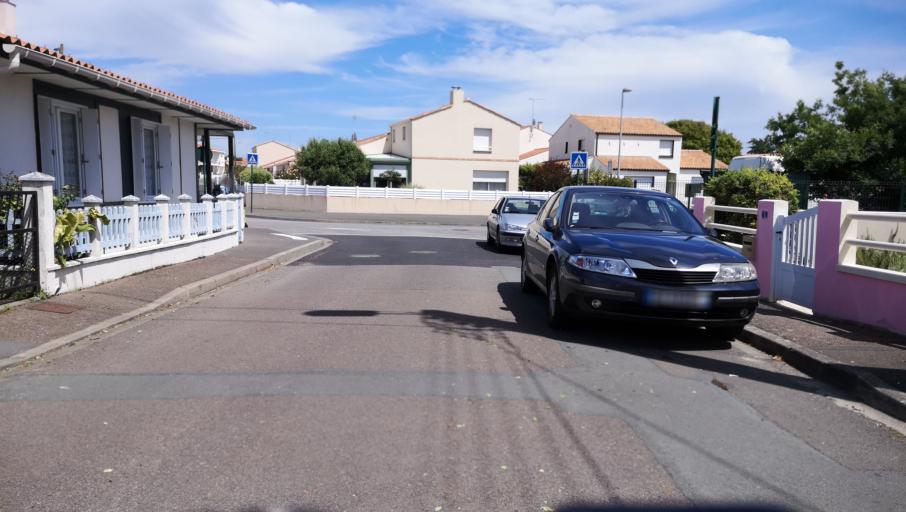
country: FR
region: Pays de la Loire
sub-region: Departement de la Vendee
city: Les Sables-d'Olonne
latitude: 46.5016
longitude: -1.7731
